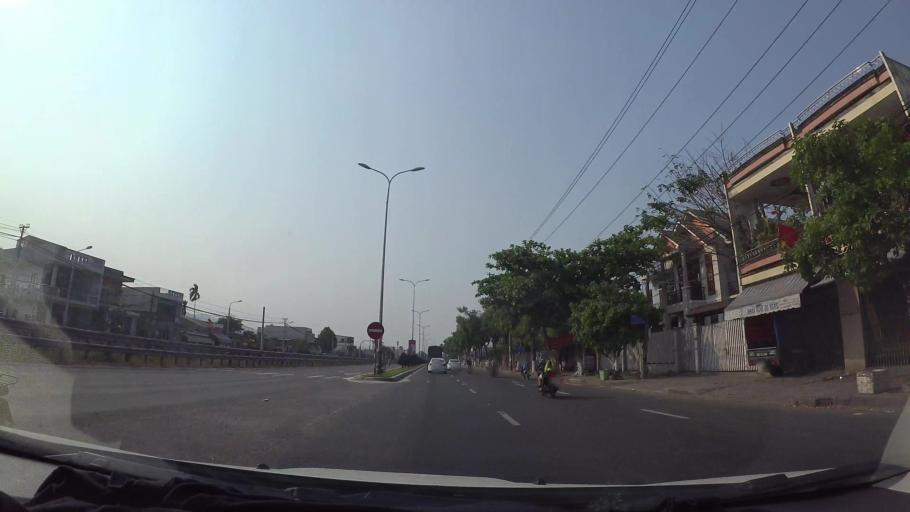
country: VN
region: Da Nang
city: Cam Le
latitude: 16.0227
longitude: 108.1928
